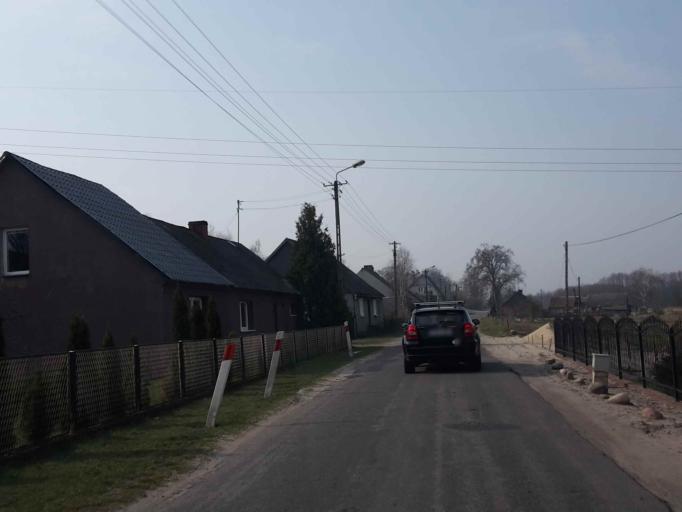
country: PL
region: Kujawsko-Pomorskie
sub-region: Powiat nakielski
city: Sadki
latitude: 53.0752
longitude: 17.4373
